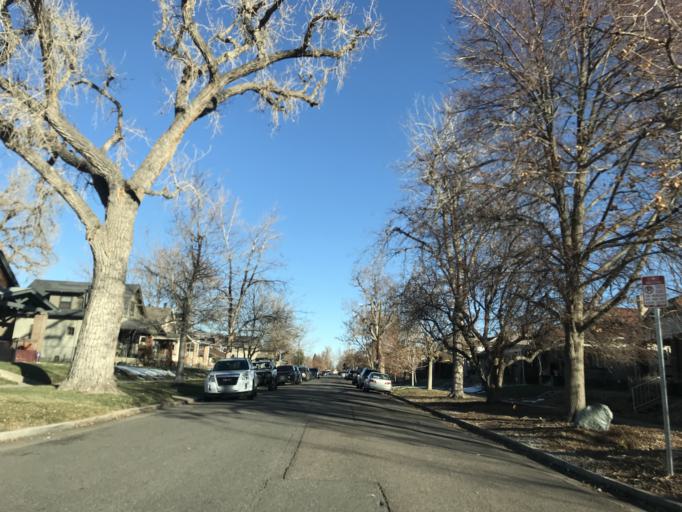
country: US
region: Colorado
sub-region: Denver County
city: Denver
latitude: 39.7621
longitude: -104.9622
